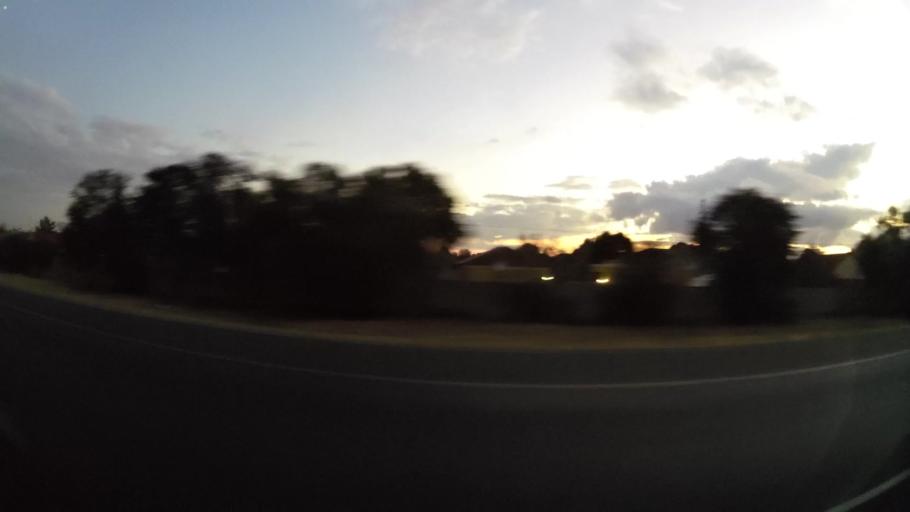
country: ZA
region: Orange Free State
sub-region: Mangaung Metropolitan Municipality
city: Bloemfontein
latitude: -29.1568
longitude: 26.1764
